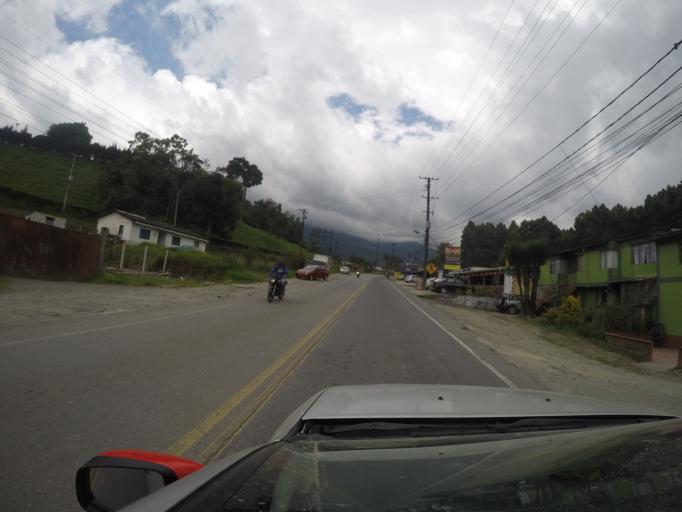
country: CO
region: Caldas
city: Villamaria
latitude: 5.0364
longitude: -75.4547
